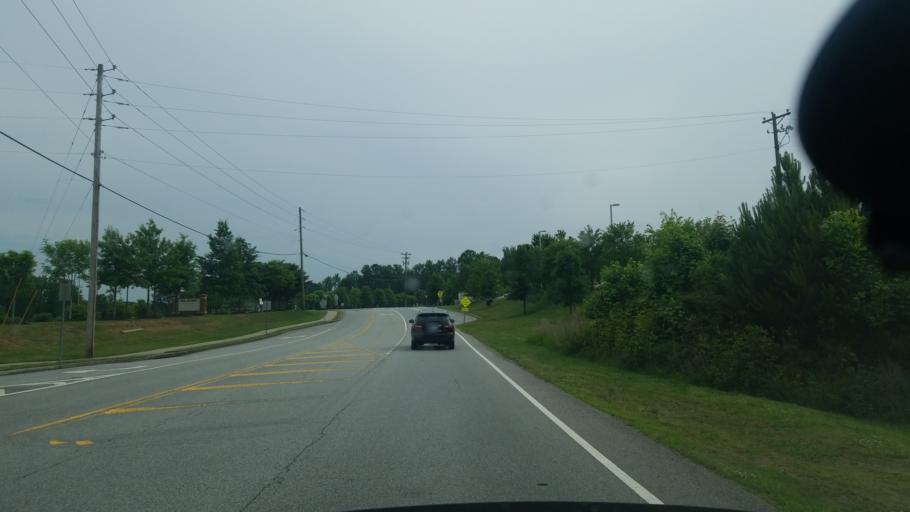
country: US
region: Georgia
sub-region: Gwinnett County
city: Suwanee
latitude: 34.1084
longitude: -84.1415
